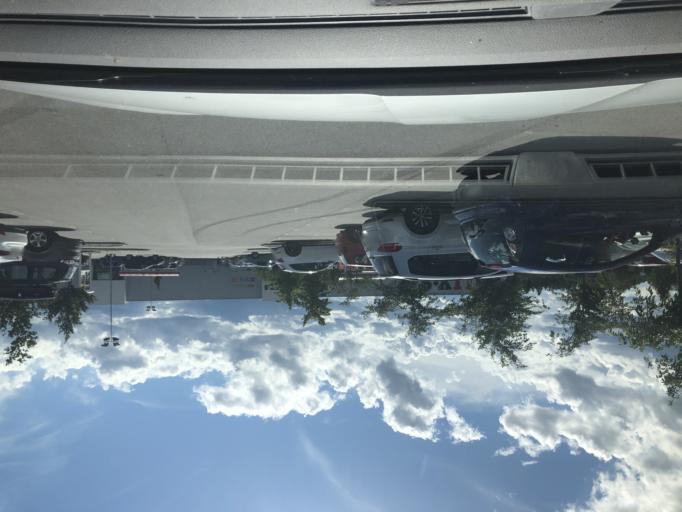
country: SE
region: Stockholm
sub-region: Jarfalla Kommun
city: Jakobsberg
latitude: 59.4094
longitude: 17.8442
